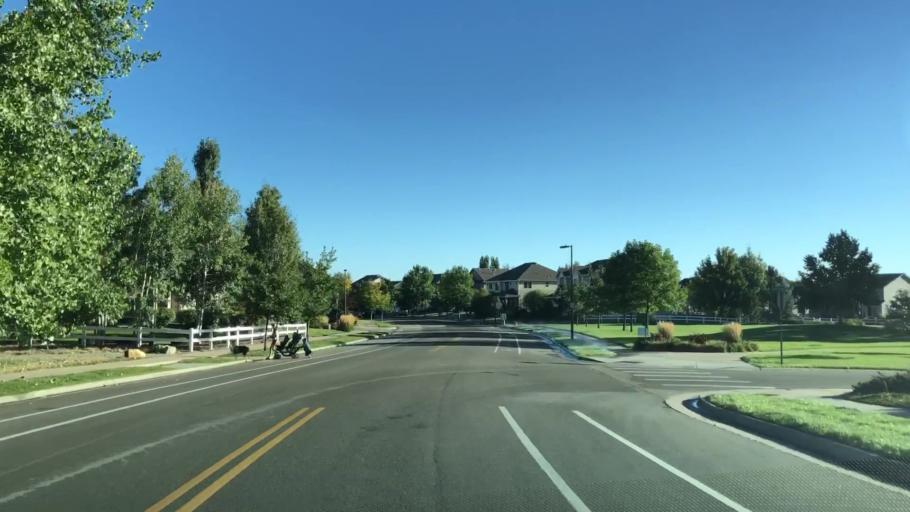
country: US
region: Colorado
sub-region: Larimer County
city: Loveland
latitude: 40.4567
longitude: -105.0321
